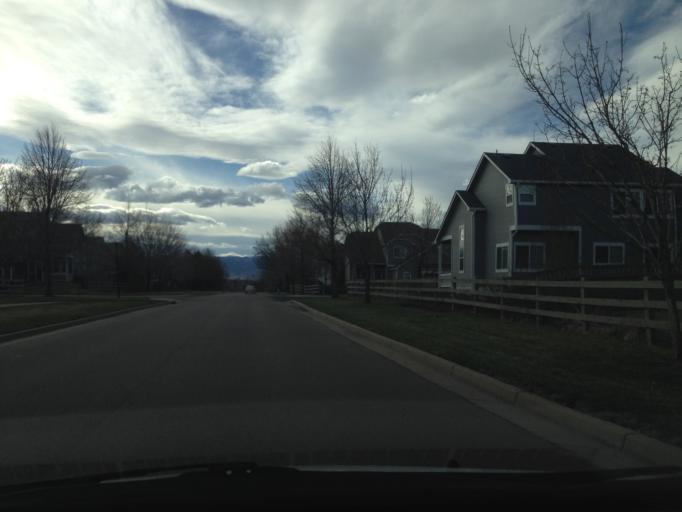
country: US
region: Colorado
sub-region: Boulder County
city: Louisville
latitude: 39.9979
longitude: -105.1207
